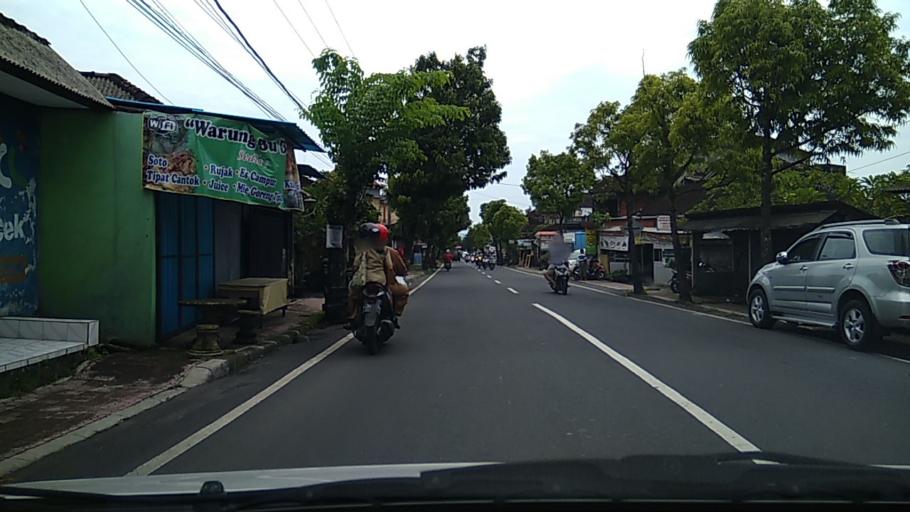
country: ID
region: Bali
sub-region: Kabupaten Gianyar
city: Ubud
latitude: -8.5313
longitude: 115.3004
